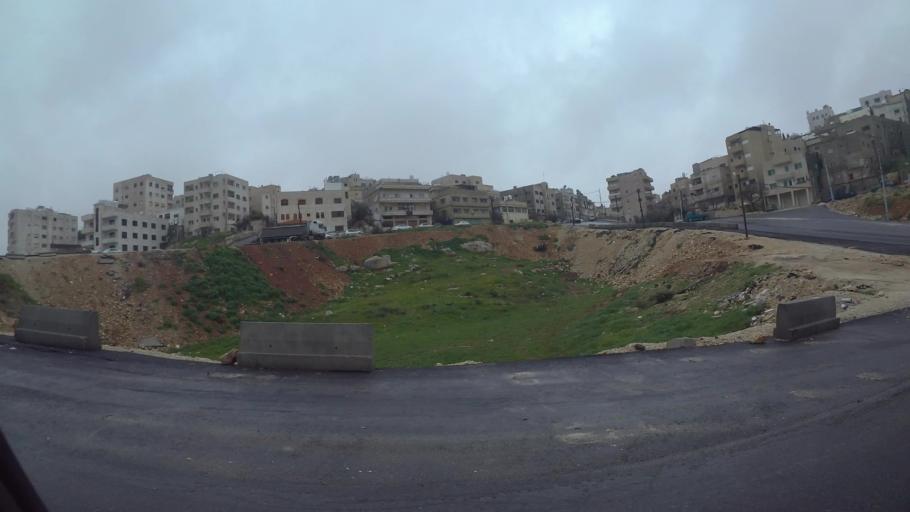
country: JO
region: Amman
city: Al Jubayhah
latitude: 32.0192
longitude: 35.8344
